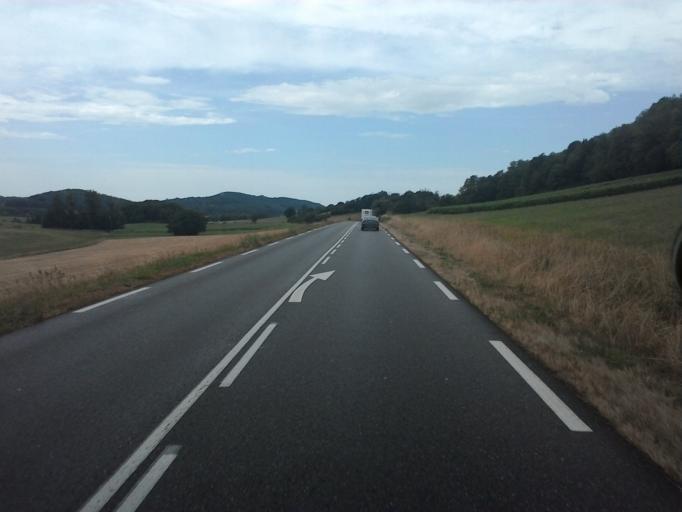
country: FR
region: Franche-Comte
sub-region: Departement du Jura
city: Poligny
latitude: 46.8272
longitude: 5.5978
